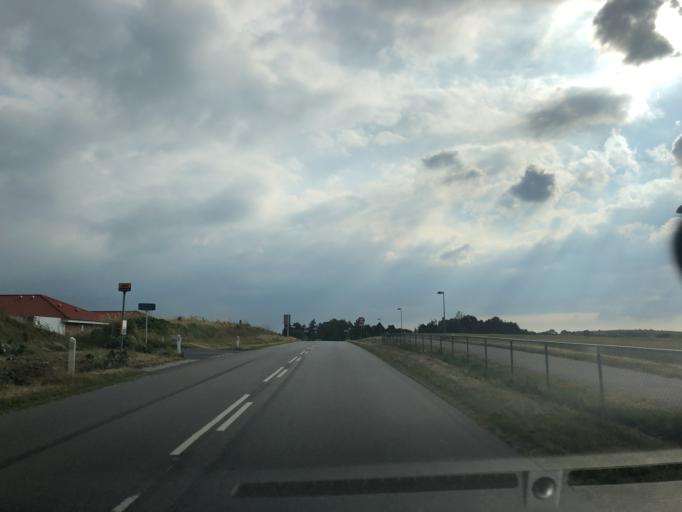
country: DK
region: Zealand
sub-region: Faxe Kommune
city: Haslev
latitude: 55.3170
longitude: 11.9632
